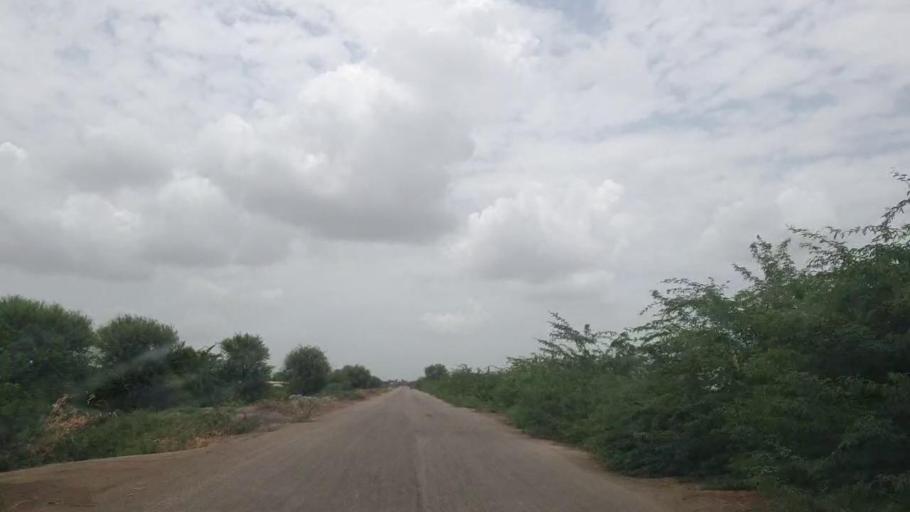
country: PK
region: Sindh
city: Naukot
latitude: 24.9237
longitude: 69.2741
